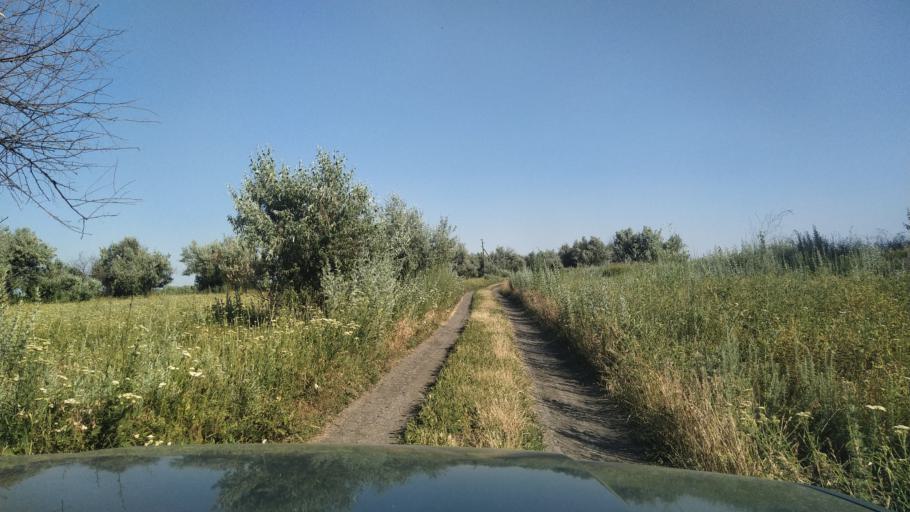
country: RU
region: Rostov
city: Kuleshovka
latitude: 47.1355
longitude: 39.6406
